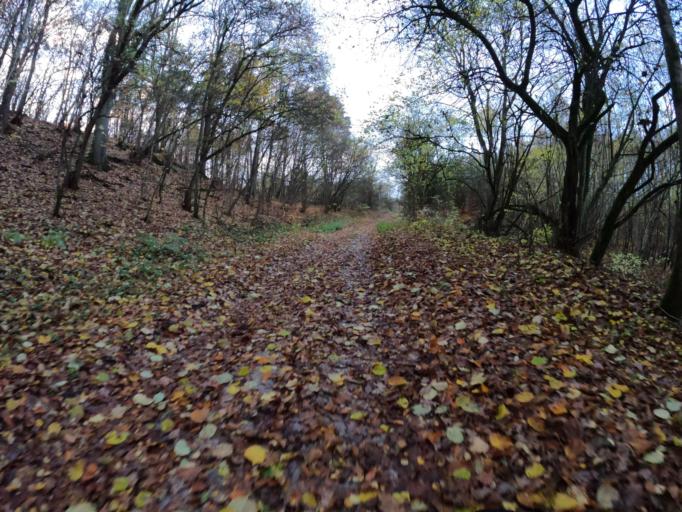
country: PL
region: West Pomeranian Voivodeship
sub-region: Powiat walecki
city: Tuczno
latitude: 53.1855
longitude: 16.1582
